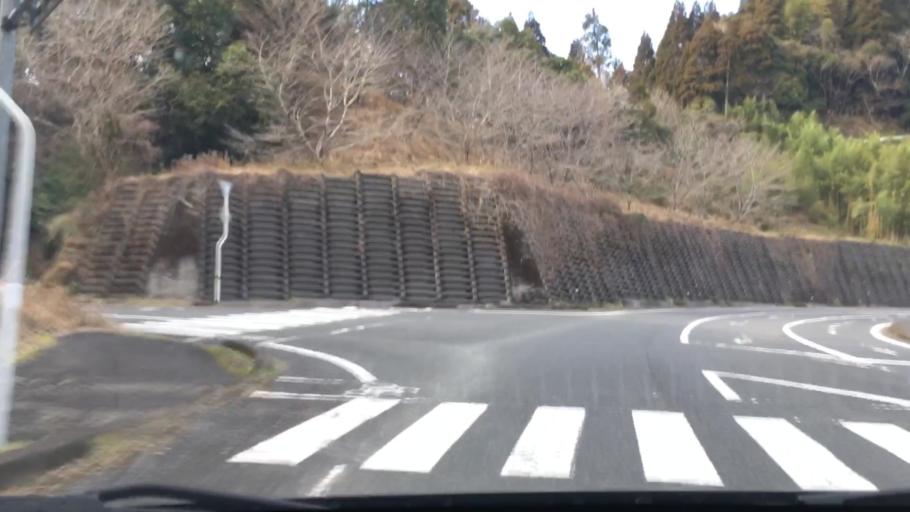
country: JP
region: Miyazaki
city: Kushima
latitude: 31.5462
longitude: 131.2418
